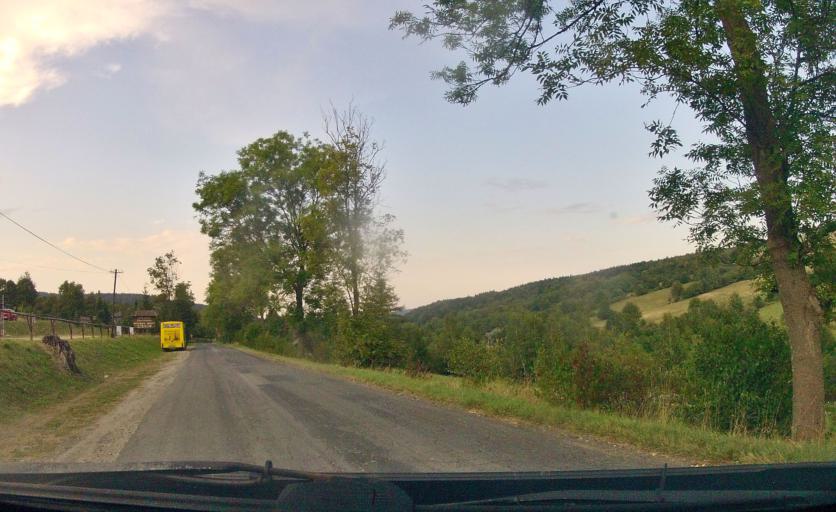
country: PL
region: Subcarpathian Voivodeship
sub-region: Powiat krosnienski
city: Dukla
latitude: 49.5322
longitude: 21.6154
